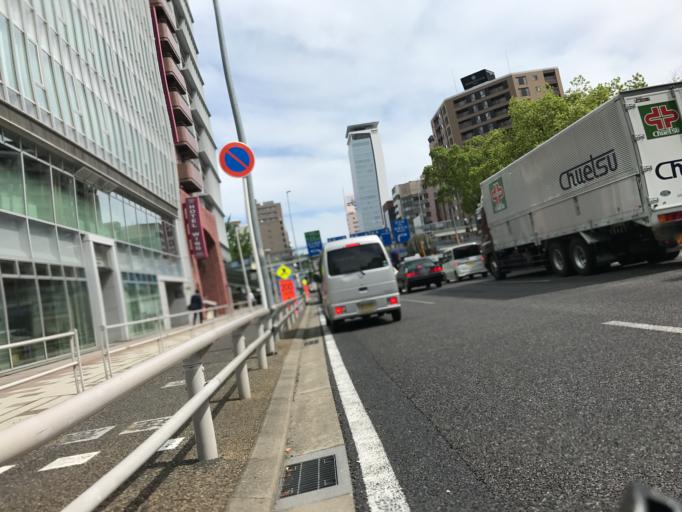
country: JP
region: Aichi
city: Nagoya-shi
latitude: 35.1719
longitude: 136.8970
